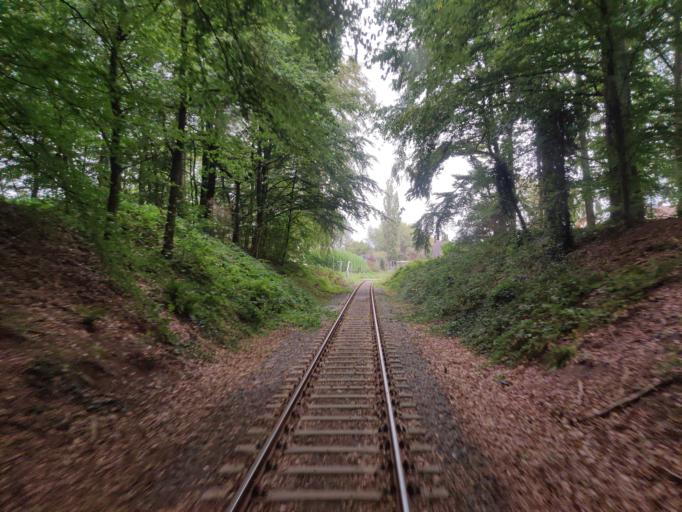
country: DE
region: Lower Saxony
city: Osterholz-Scharmbeck
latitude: 53.2316
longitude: 8.8055
